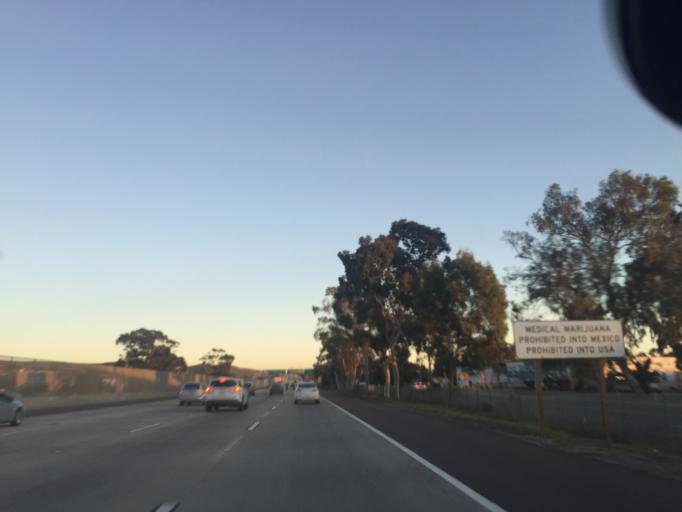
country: US
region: California
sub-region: San Diego County
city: Imperial Beach
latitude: 32.5538
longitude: -117.0515
